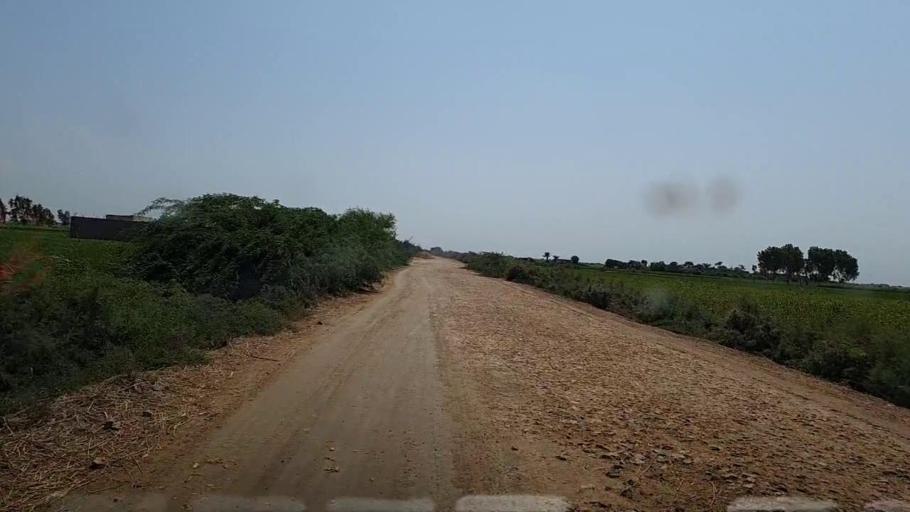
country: PK
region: Sindh
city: Mirpur Batoro
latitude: 24.6263
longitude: 68.4522
